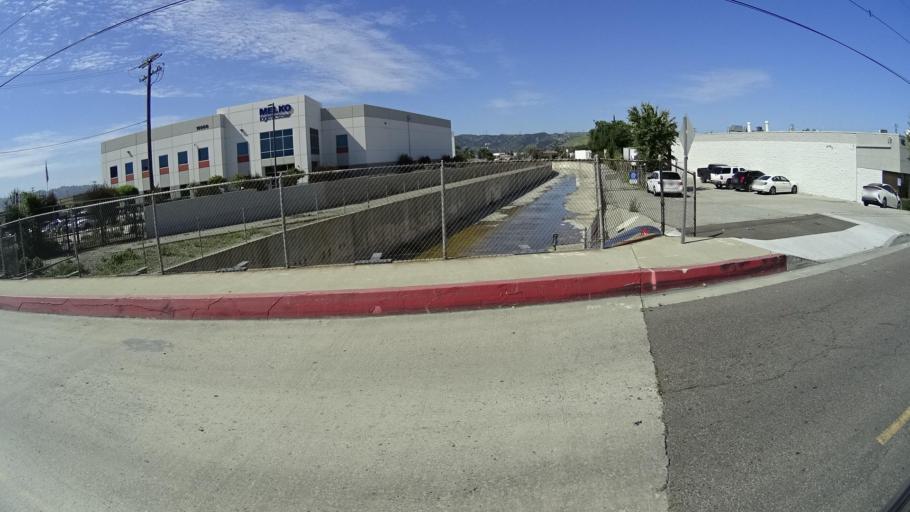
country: US
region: California
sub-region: Los Angeles County
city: West Puente Valley
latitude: 34.0324
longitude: -117.9660
